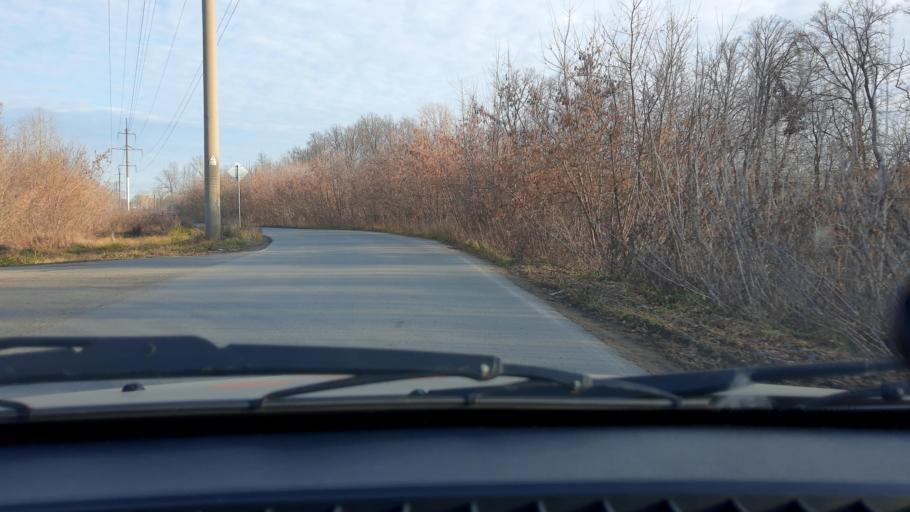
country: RU
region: Bashkortostan
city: Ufa
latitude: 54.6649
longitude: 55.9507
